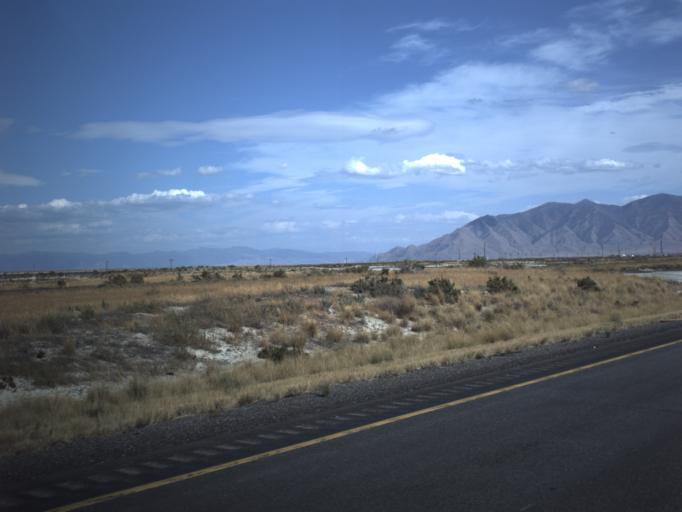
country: US
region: Utah
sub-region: Tooele County
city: Grantsville
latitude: 40.6933
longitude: -112.4695
